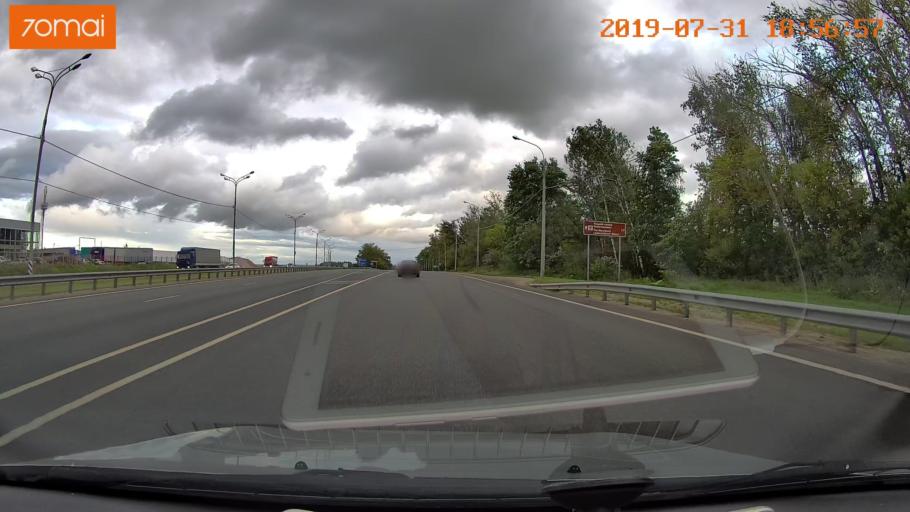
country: RU
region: Moskovskaya
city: Raduzhnyy
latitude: 55.1583
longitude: 38.6854
